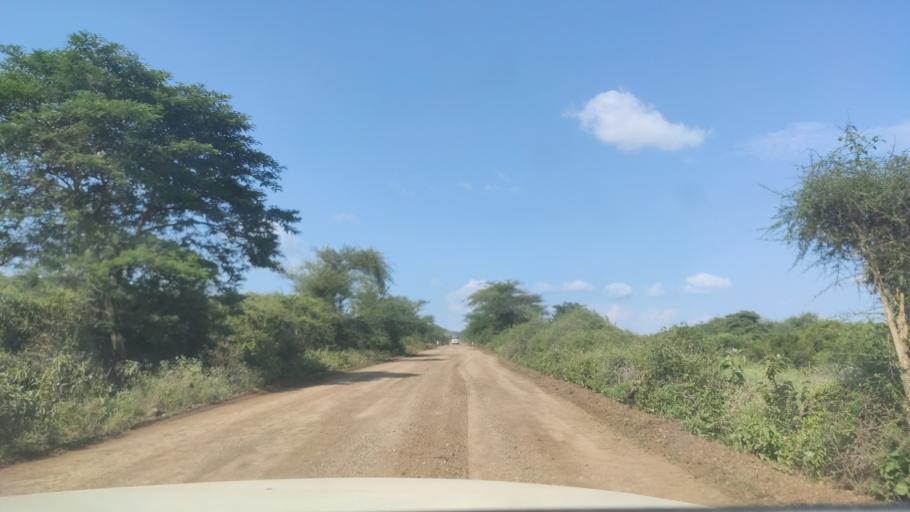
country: ET
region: Southern Nations, Nationalities, and People's Region
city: Felege Neway
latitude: 6.3897
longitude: 37.0980
